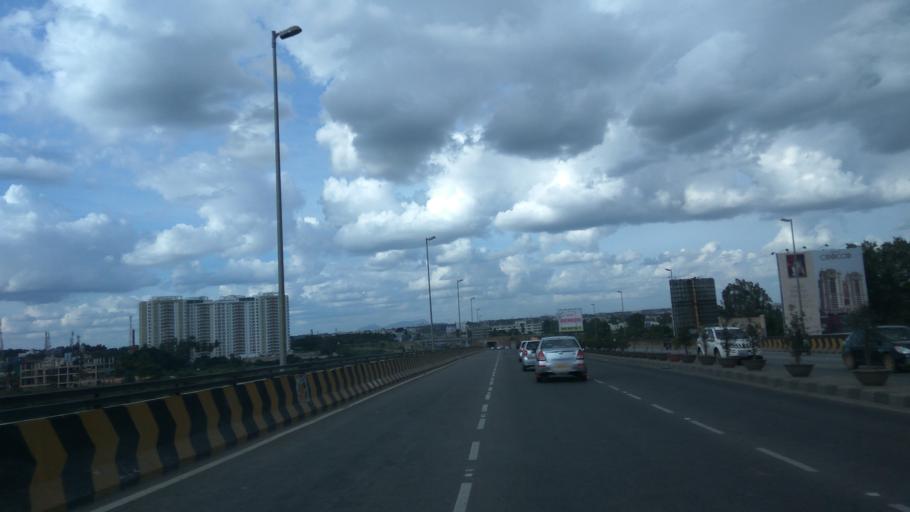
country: IN
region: Karnataka
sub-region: Bangalore Urban
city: Yelahanka
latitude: 13.0869
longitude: 77.5950
